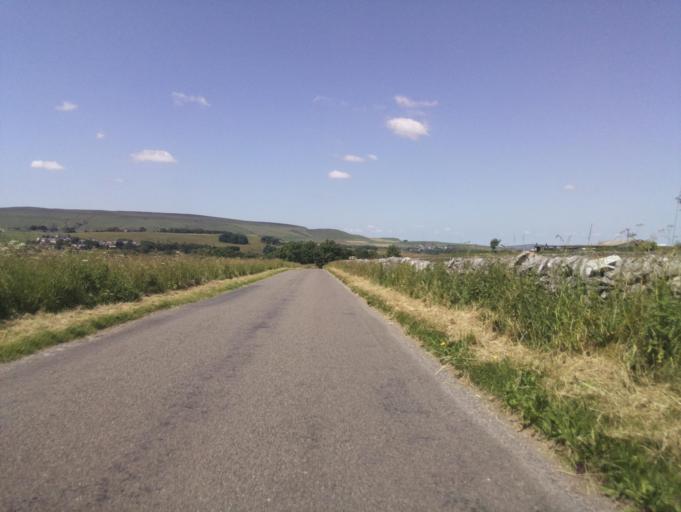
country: GB
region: England
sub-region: Derbyshire
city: Buxton
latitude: 53.2842
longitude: -1.8547
